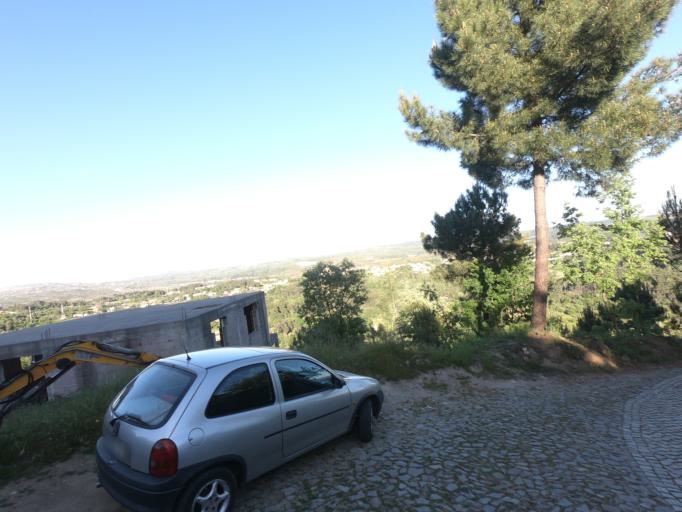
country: PT
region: Vila Real
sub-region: Vila Real
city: Vila Real
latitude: 41.3456
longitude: -7.7376
